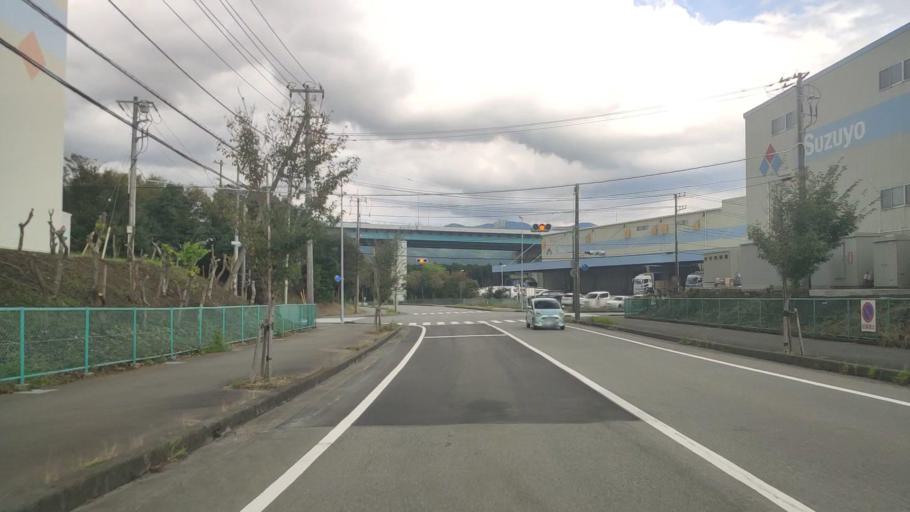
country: JP
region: Shizuoka
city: Gotemba
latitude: 35.2712
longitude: 138.9082
